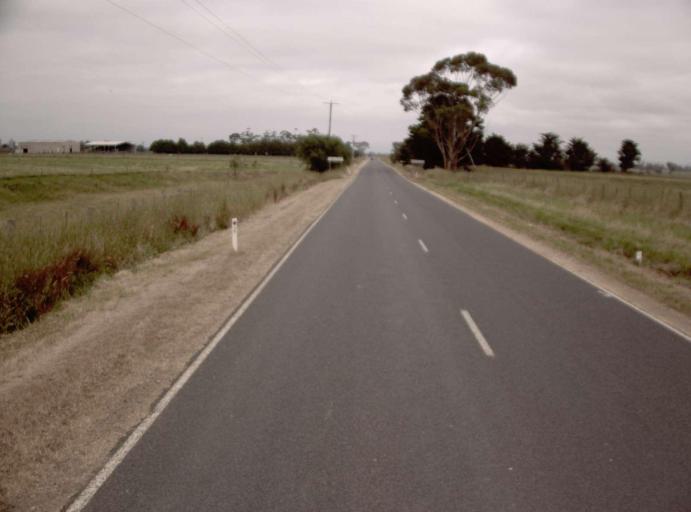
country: AU
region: Victoria
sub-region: Wellington
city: Heyfield
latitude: -38.0349
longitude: 146.9241
